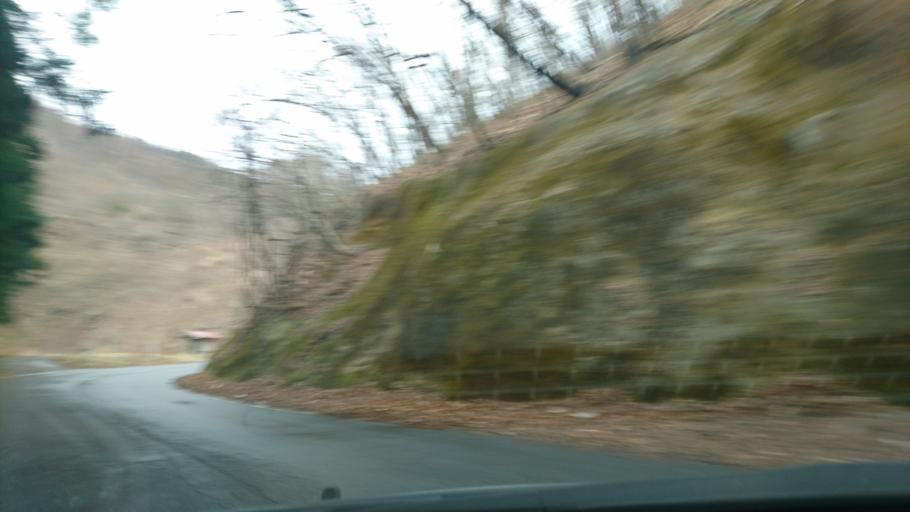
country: JP
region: Iwate
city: Ofunato
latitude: 38.9955
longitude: 141.5477
